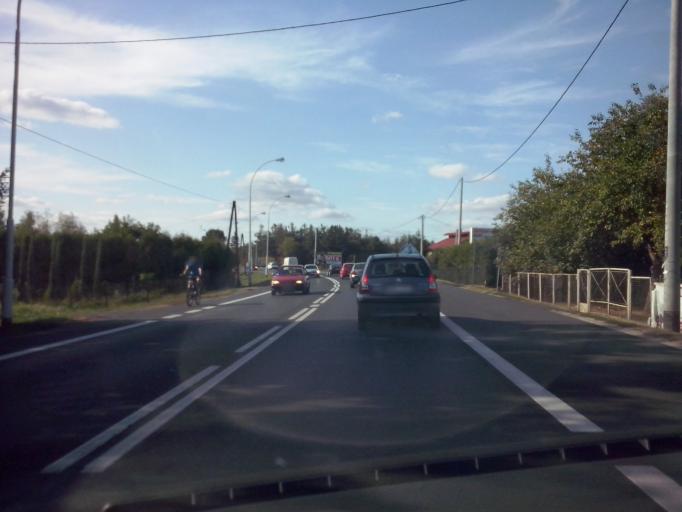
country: PL
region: Subcarpathian Voivodeship
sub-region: Powiat nizanski
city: Nisko
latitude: 50.5374
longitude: 22.1009
